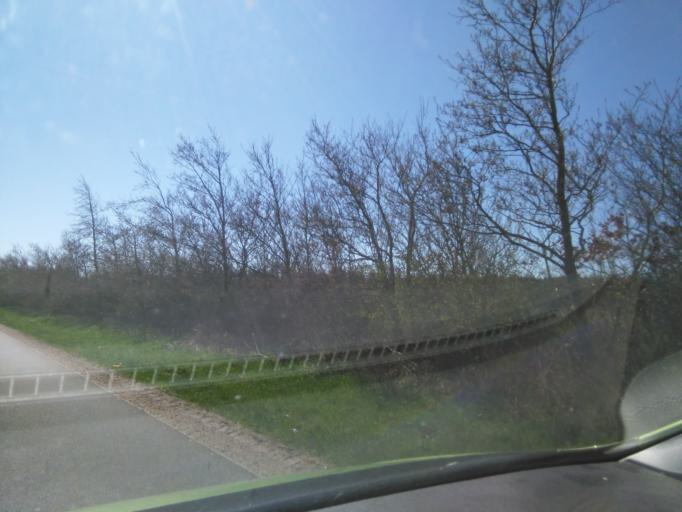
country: DK
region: South Denmark
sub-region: Varde Kommune
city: Oksbol
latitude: 55.5654
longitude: 8.2251
